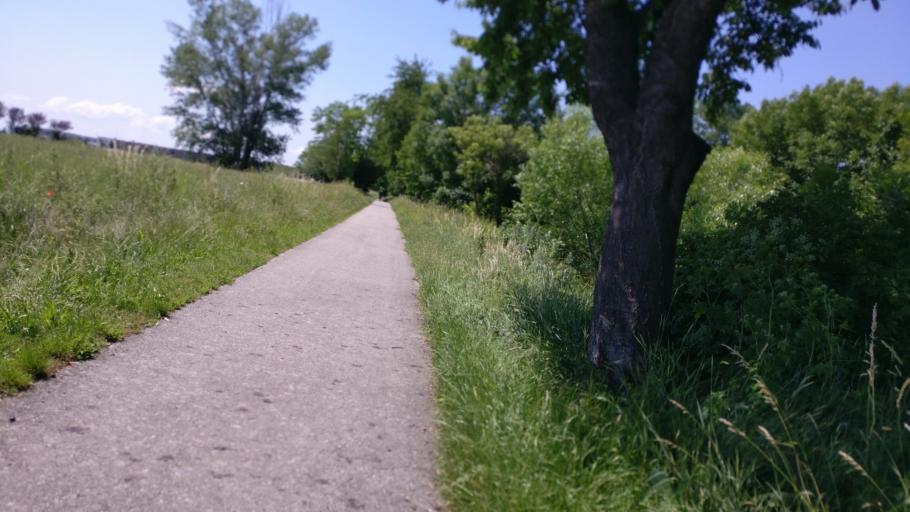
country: AT
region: Lower Austria
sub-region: Politischer Bezirk Baden
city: Trumau
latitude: 47.9886
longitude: 16.3387
